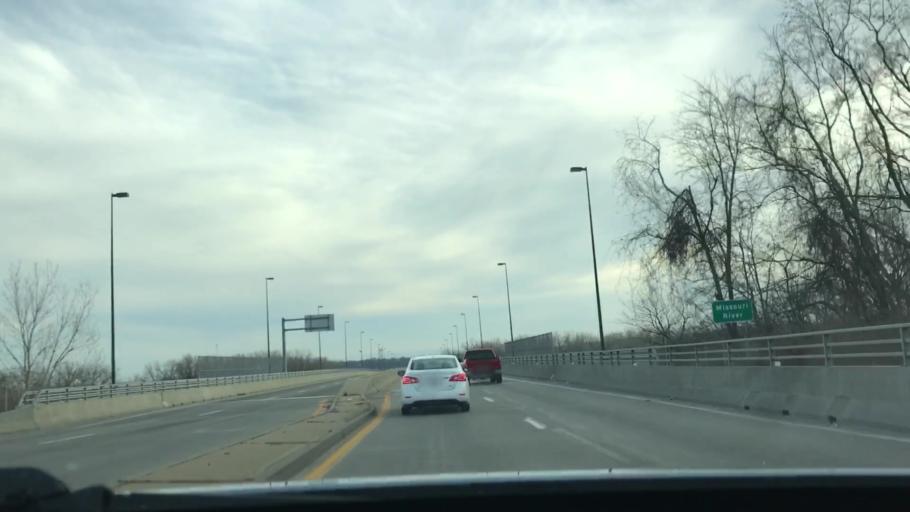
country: US
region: Missouri
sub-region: Clay County
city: North Kansas City
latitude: 39.1481
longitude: -94.5351
